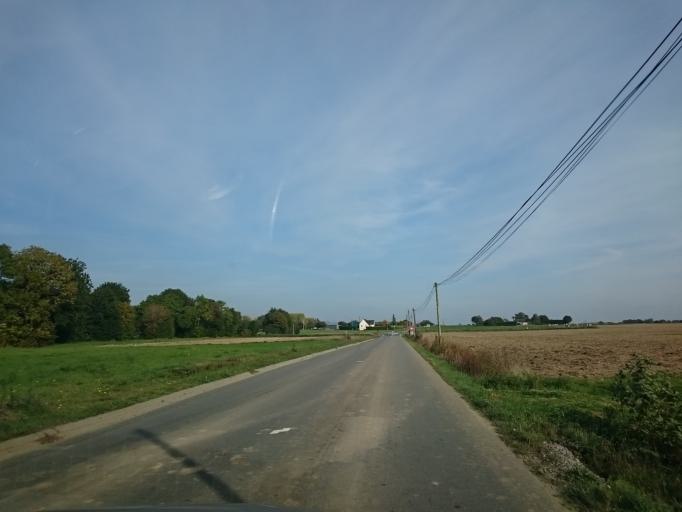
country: FR
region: Brittany
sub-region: Departement d'Ille-et-Vilaine
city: Corps-Nuds
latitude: 47.9484
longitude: -1.5702
